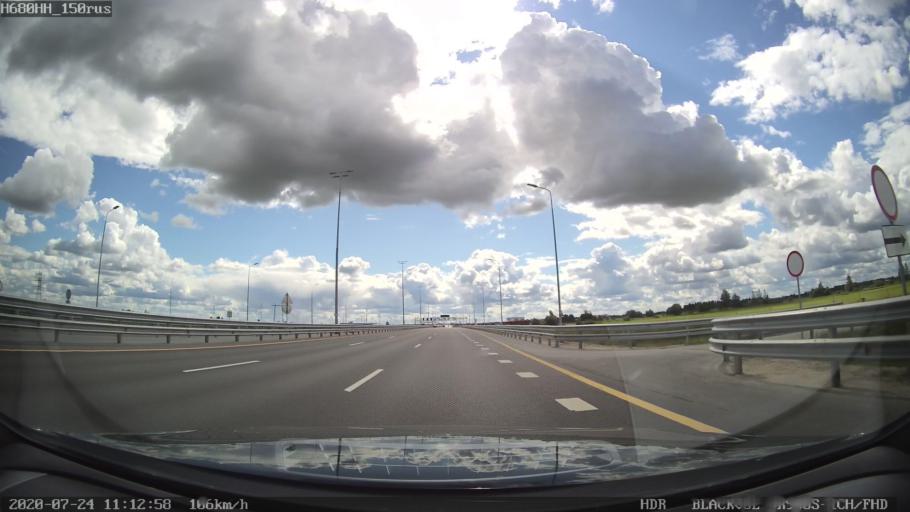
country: RU
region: Leningrad
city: Fedorovskoye
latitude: 59.7050
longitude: 30.5464
